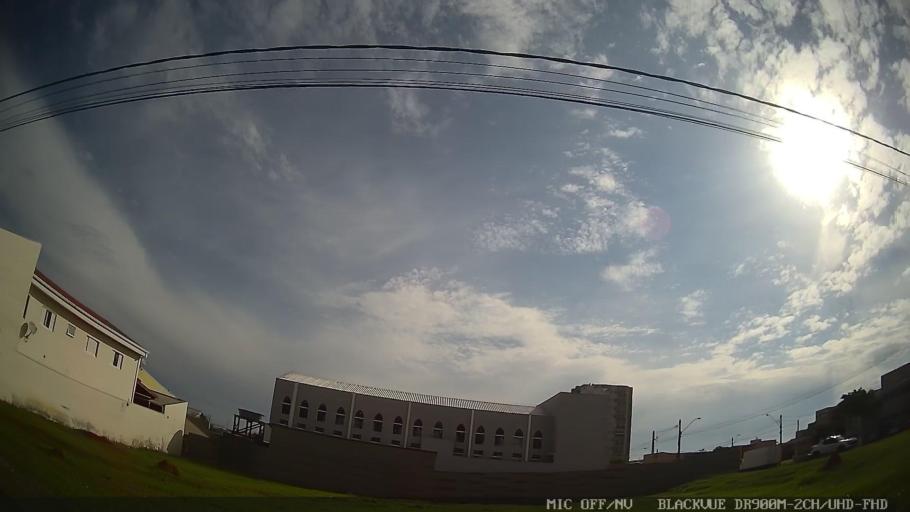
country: BR
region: Sao Paulo
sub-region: Salto
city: Salto
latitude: -23.1801
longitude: -47.2619
